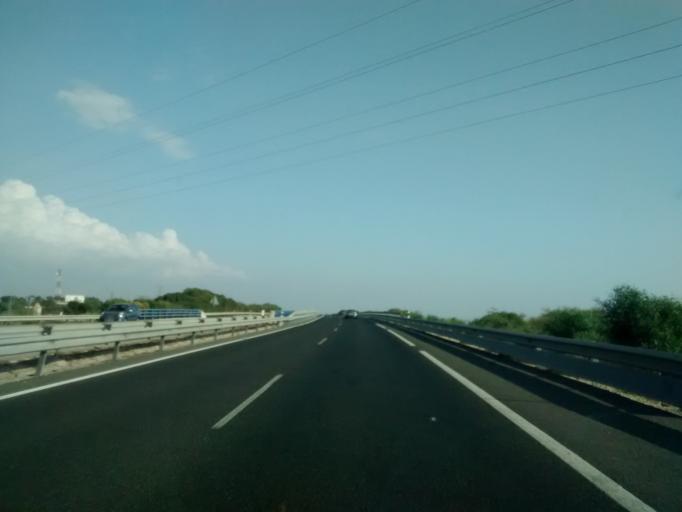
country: ES
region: Andalusia
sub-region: Provincia de Cadiz
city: Puerto Real
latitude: 36.5227
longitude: -6.1628
